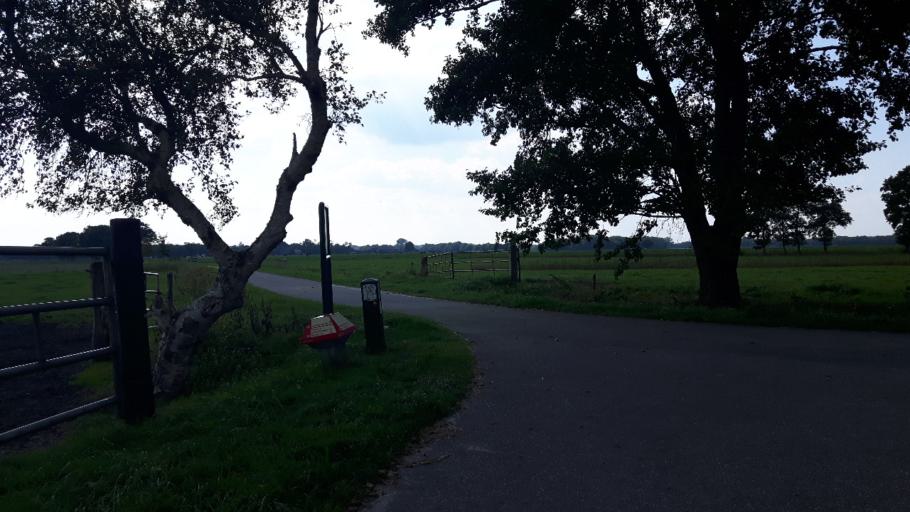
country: NL
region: Groningen
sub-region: Gemeente Leek
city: Leek
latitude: 53.1647
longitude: 6.4324
